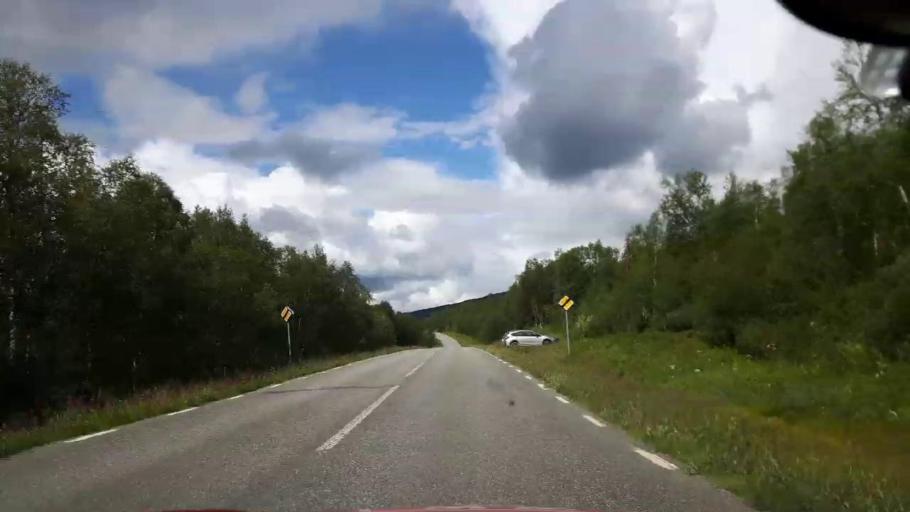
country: NO
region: Nordland
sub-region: Hattfjelldal
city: Hattfjelldal
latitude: 65.0515
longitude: 14.7417
